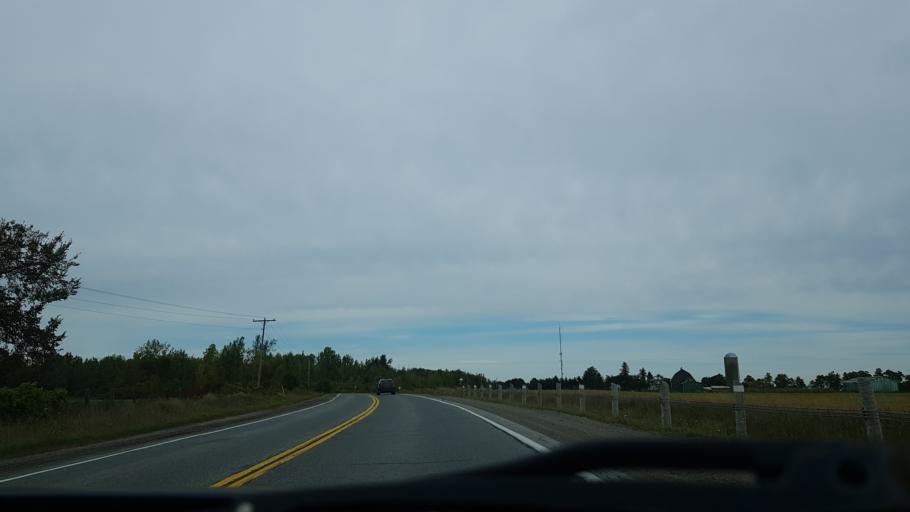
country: CA
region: Ontario
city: Orangeville
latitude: 43.9020
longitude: -79.9489
